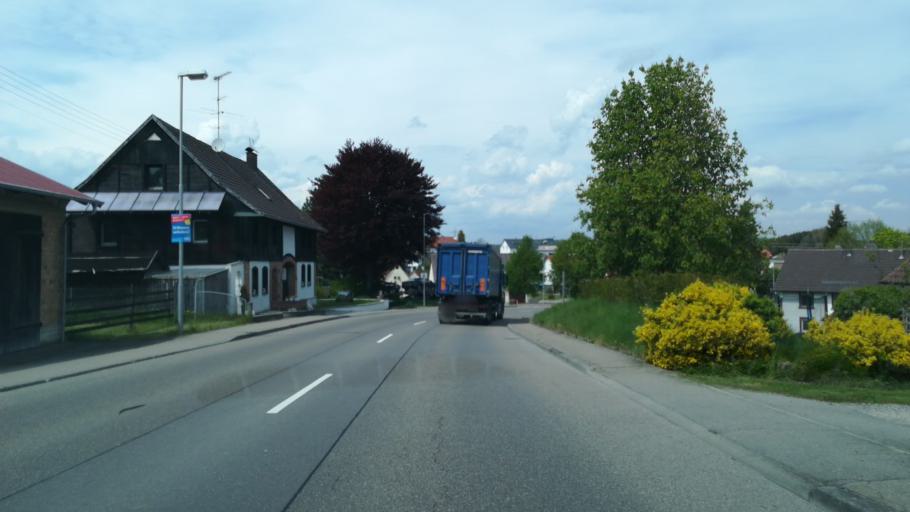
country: DE
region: Baden-Wuerttemberg
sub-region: Freiburg Region
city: Muhlingen
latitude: 47.9607
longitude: 9.0445
